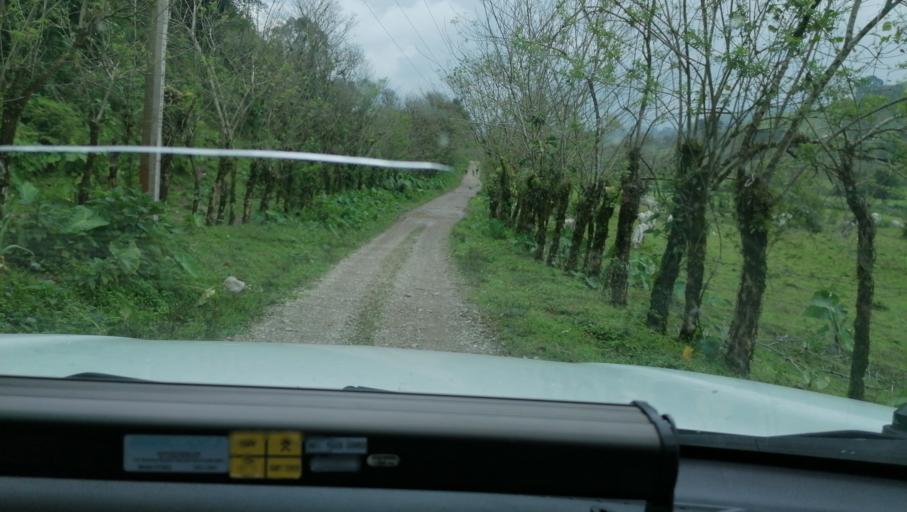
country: MX
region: Chiapas
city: Ixtacomitan
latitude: 17.3521
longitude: -93.1602
